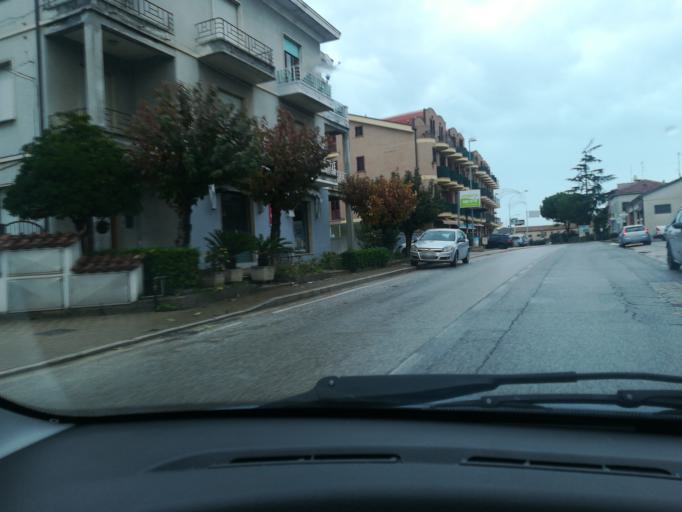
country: IT
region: The Marches
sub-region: Provincia di Macerata
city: Borgo Stazione
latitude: 43.2865
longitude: 13.6473
